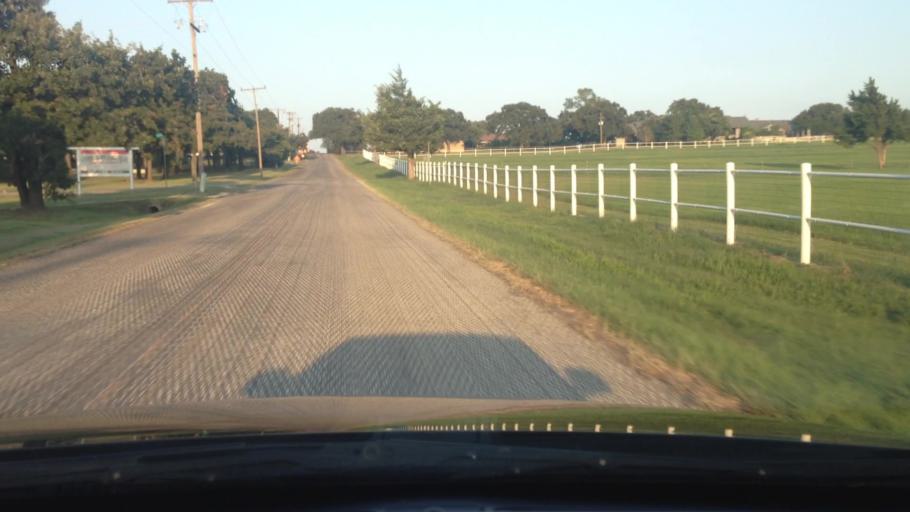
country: US
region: Texas
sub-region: Tarrant County
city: Rendon
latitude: 32.6016
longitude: -97.2368
